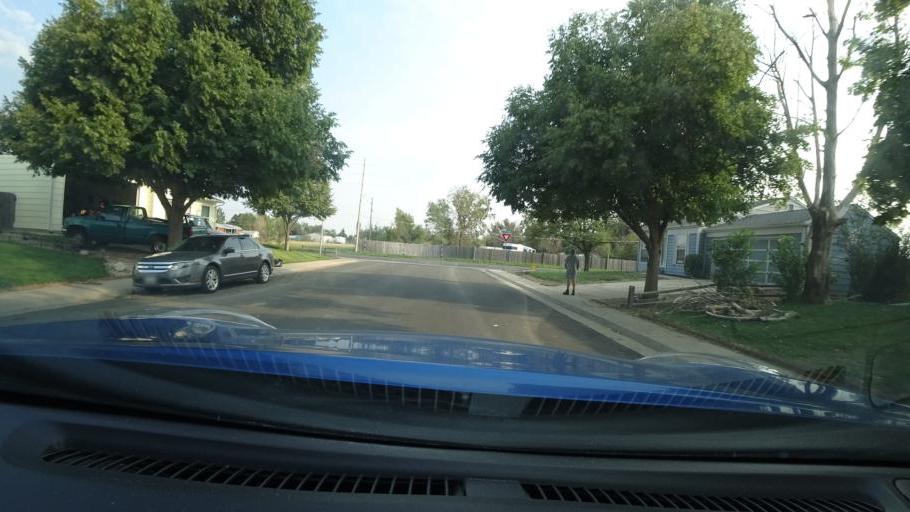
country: US
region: Colorado
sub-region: Adams County
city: Aurora
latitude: 39.7442
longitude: -104.7644
